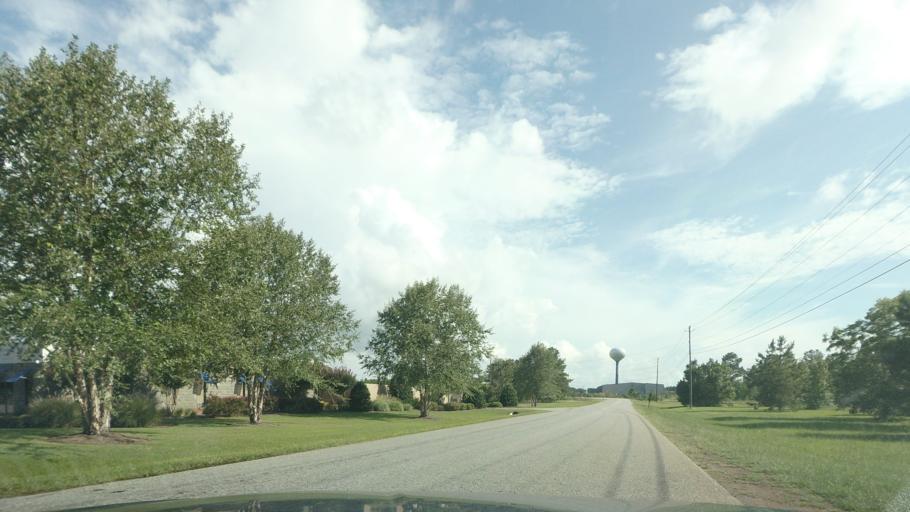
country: US
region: Georgia
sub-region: Peach County
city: Byron
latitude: 32.6514
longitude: -83.7412
